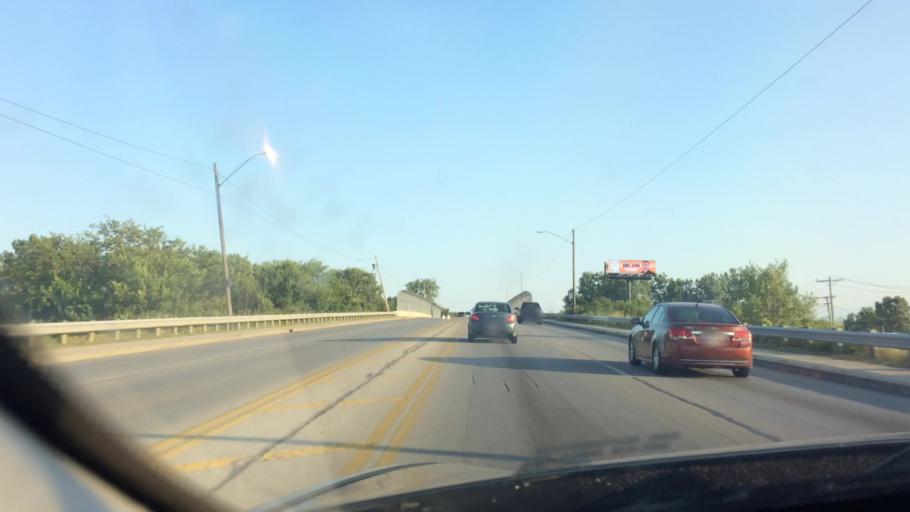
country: US
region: Ohio
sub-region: Lucas County
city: Ottawa Hills
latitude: 41.6331
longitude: -83.6259
